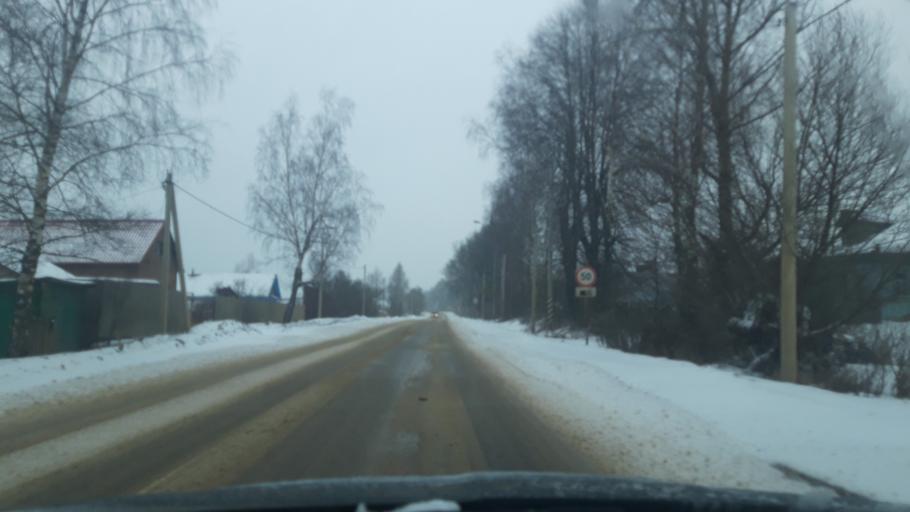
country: RU
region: Moskovskaya
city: Avtopoligon
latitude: 56.2532
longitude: 37.2308
